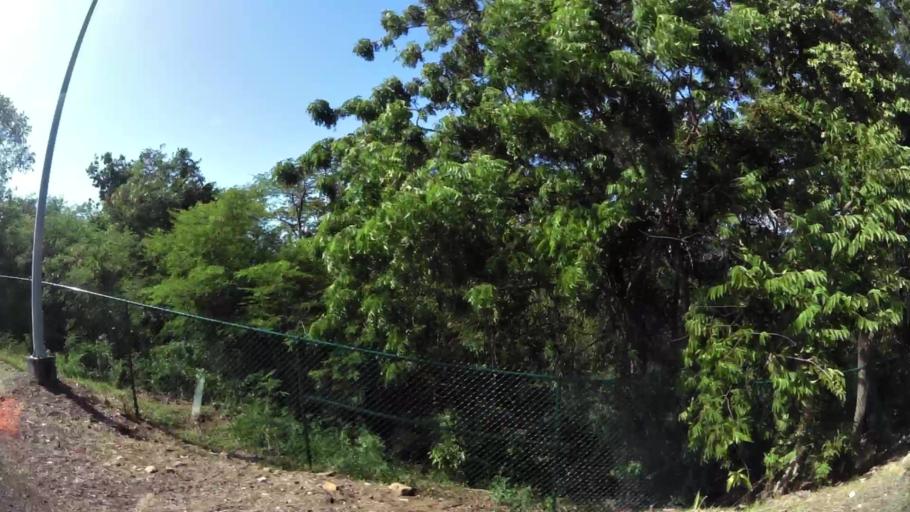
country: AG
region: Saint Paul
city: Falmouth
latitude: 17.0112
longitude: -61.7609
